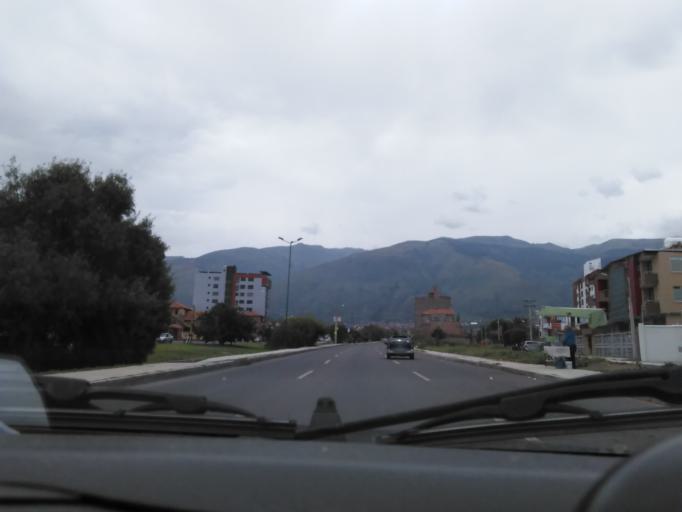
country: BO
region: Cochabamba
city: Cochabamba
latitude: -17.3680
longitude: -66.1792
